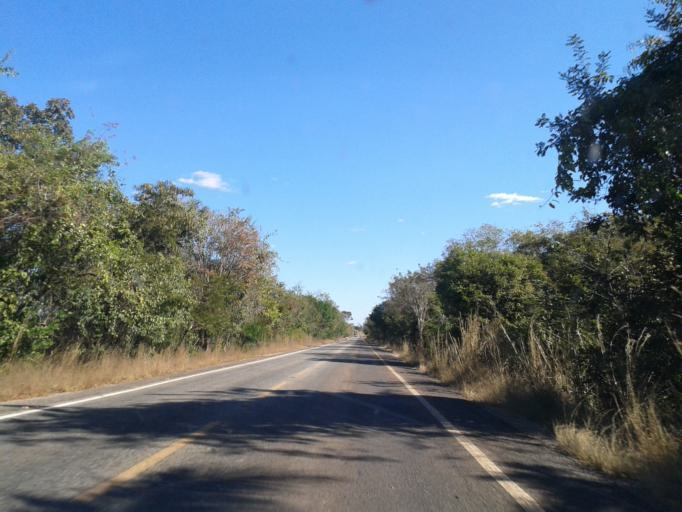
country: BR
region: Goias
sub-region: Mozarlandia
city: Mozarlandia
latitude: -14.4870
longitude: -50.4801
